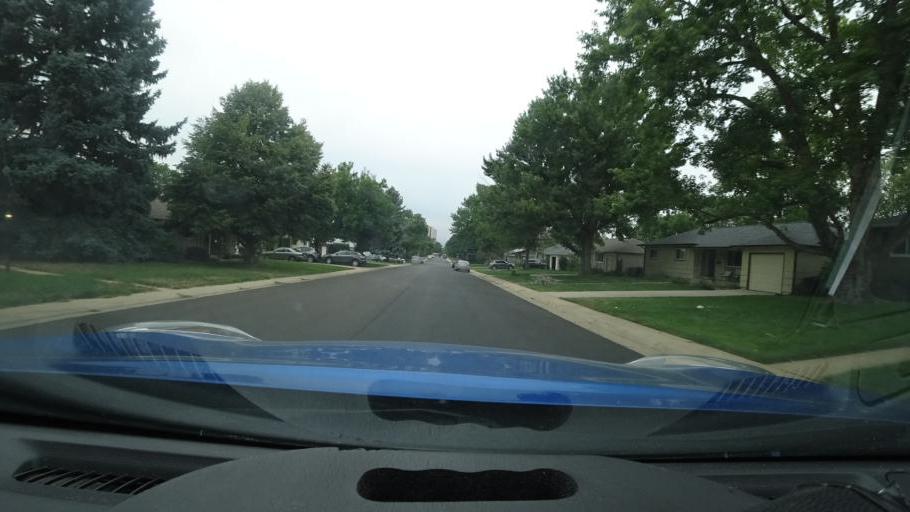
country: US
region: Colorado
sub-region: Arapahoe County
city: Glendale
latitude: 39.6813
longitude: -104.9270
